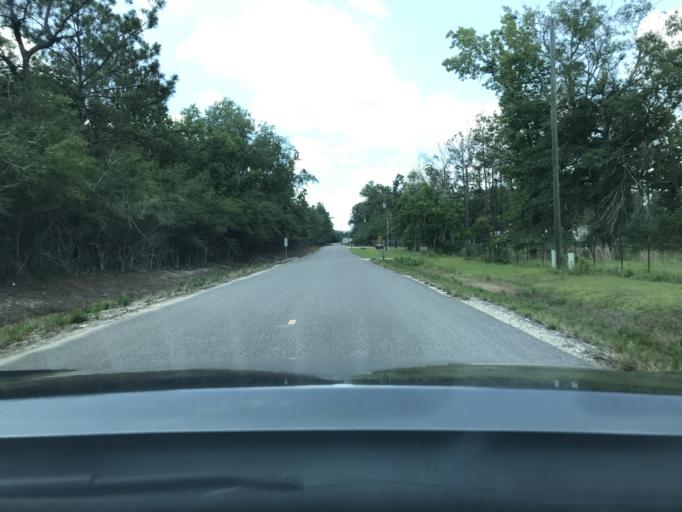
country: US
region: Louisiana
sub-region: Calcasieu Parish
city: Moss Bluff
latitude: 30.3313
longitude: -93.1308
